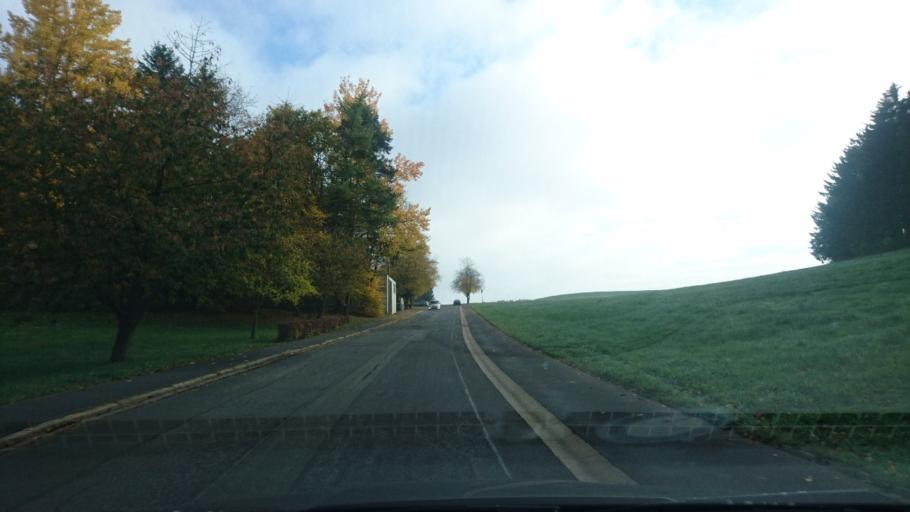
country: DE
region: Bavaria
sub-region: Upper Franconia
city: Selbitz
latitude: 50.3155
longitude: 11.7547
